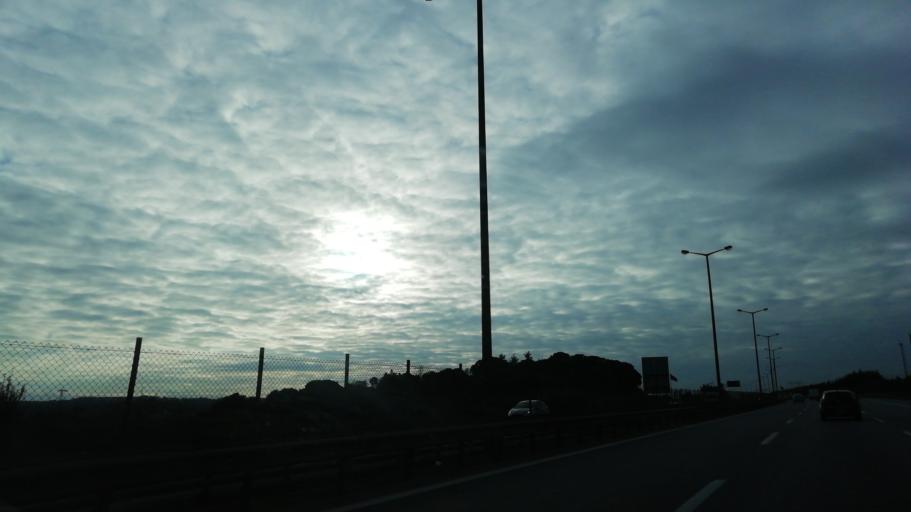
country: TR
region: Istanbul
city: Icmeler
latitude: 40.9230
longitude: 29.3509
